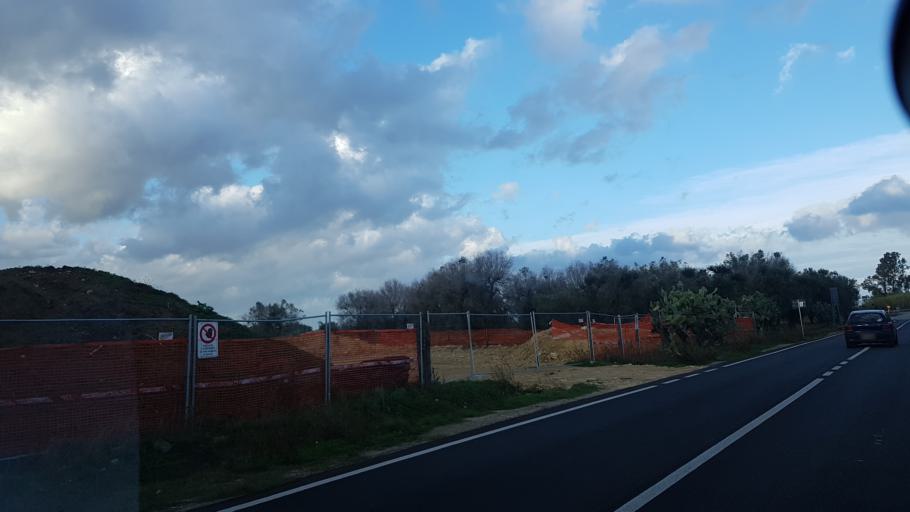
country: IT
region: Apulia
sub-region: Provincia di Brindisi
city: San Pietro Vernotico
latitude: 40.5180
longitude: 18.0134
